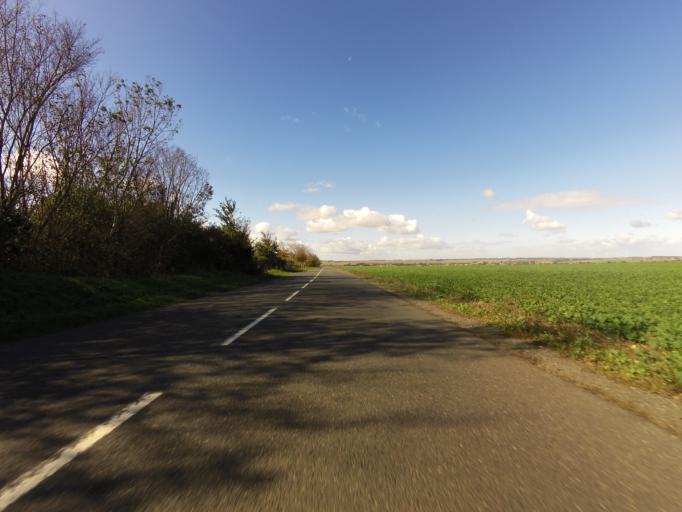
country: FR
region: Lower Normandy
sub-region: Departement du Calvados
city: Saint-Sylvain
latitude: 49.0513
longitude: -0.1811
